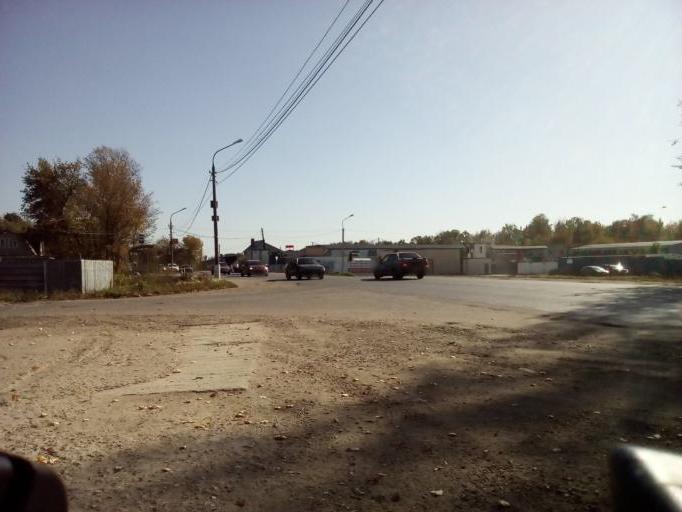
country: RU
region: Moskovskaya
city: Ramenskoye
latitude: 55.5439
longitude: 38.2937
